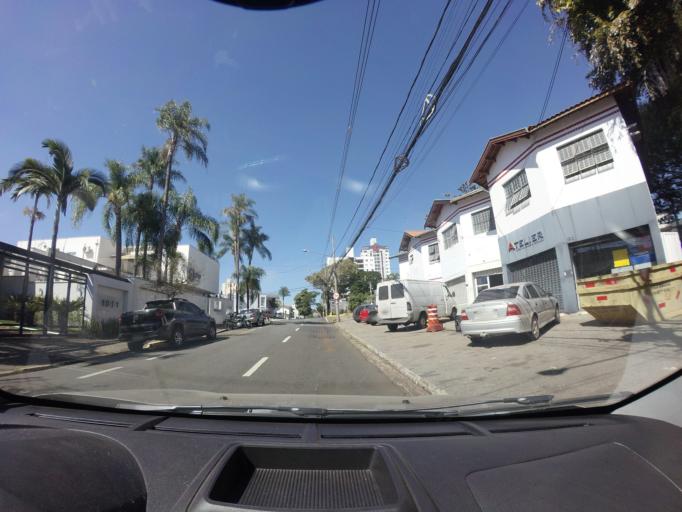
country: BR
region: Sao Paulo
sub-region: Piracicaba
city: Piracicaba
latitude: -22.7194
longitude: -47.6432
